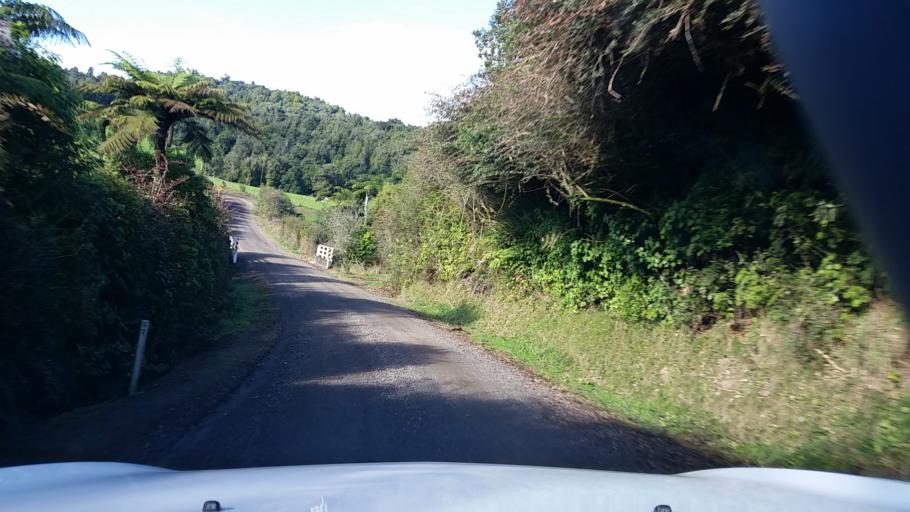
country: NZ
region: Waikato
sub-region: Matamata-Piako District
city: Matamata
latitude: -37.8245
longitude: 175.6278
